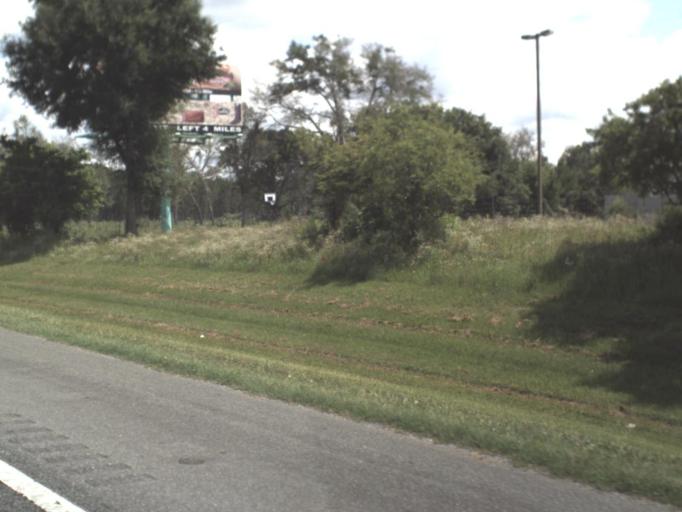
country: US
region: Florida
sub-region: Columbia County
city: Lake City
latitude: 30.1337
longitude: -82.6648
